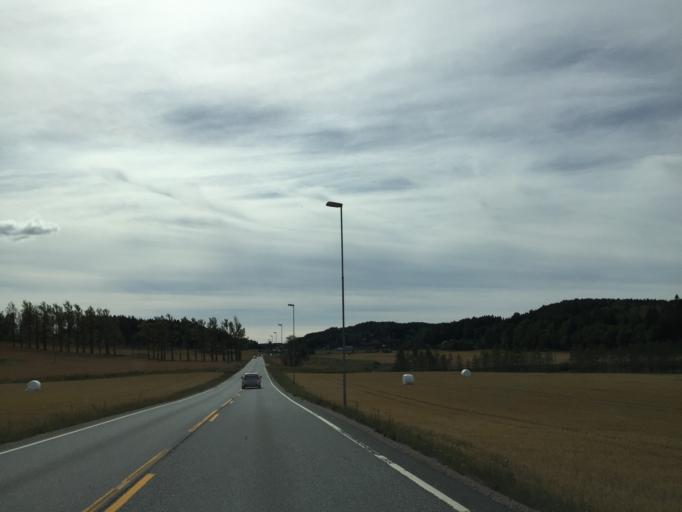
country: NO
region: Ostfold
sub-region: Fredrikstad
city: Fredrikstad
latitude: 59.2600
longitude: 10.8925
